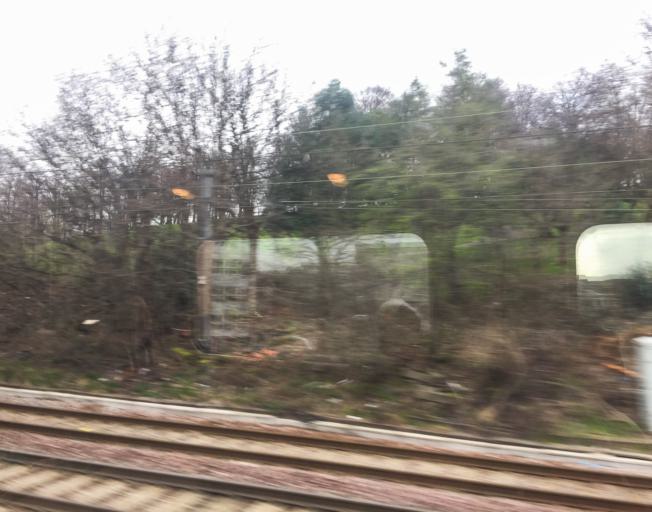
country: GB
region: Scotland
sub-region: West Dunbartonshire
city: Duntocher
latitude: 55.9122
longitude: -4.4279
